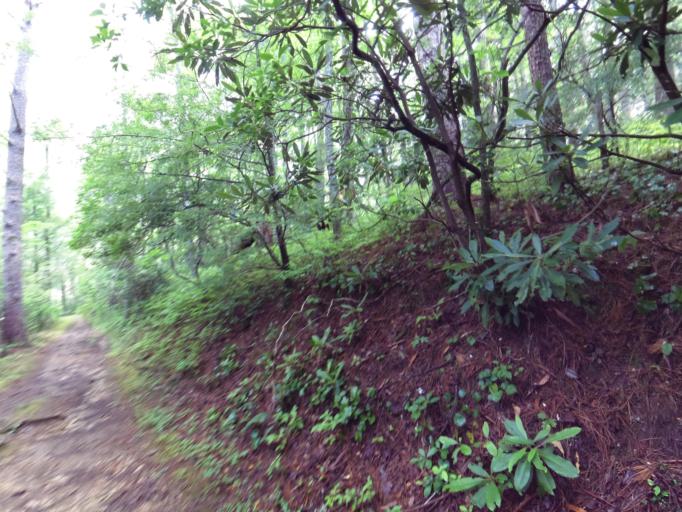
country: US
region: Tennessee
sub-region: Blount County
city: Wildwood
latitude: 35.6026
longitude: -83.7614
